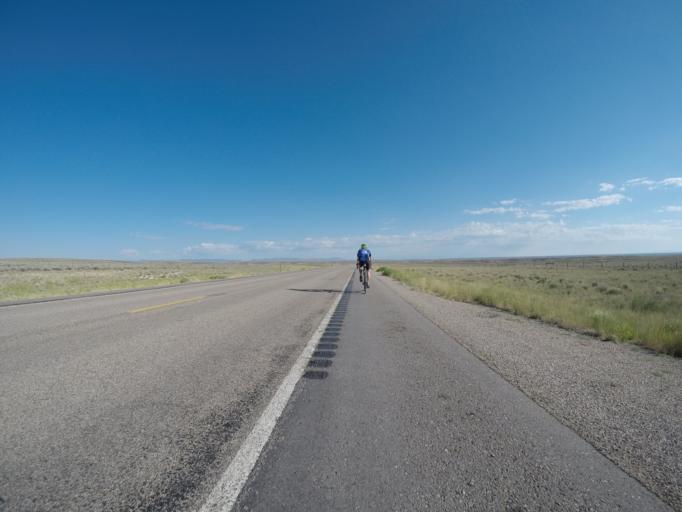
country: US
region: Wyoming
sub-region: Lincoln County
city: Kemmerer
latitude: 42.0351
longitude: -110.1557
